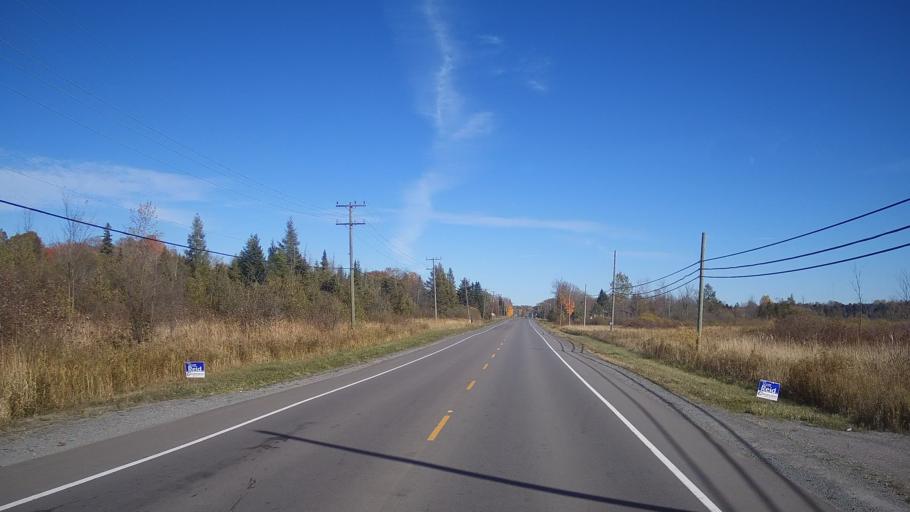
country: CA
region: Ontario
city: Kingston
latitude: 44.4059
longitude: -76.6276
